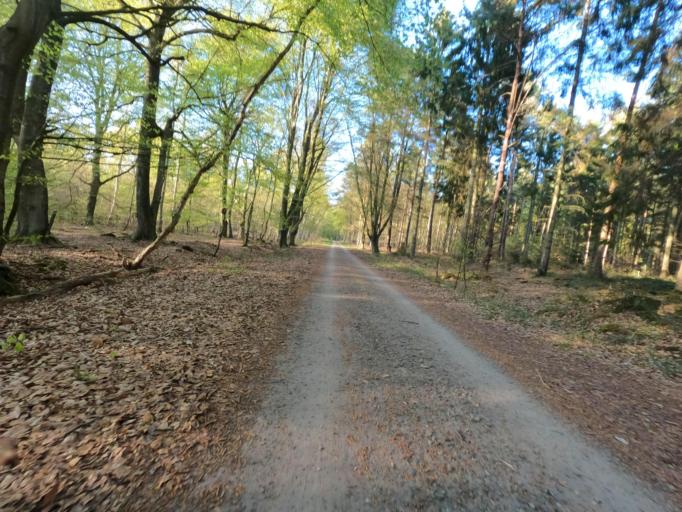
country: DE
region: Mecklenburg-Vorpommern
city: Born
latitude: 54.4224
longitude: 12.5355
